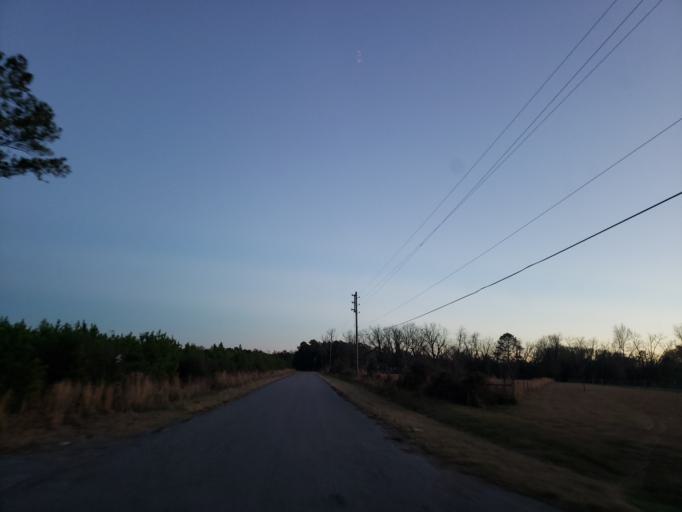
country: US
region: Mississippi
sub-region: Forrest County
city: Rawls Springs
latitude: 31.4451
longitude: -89.3864
